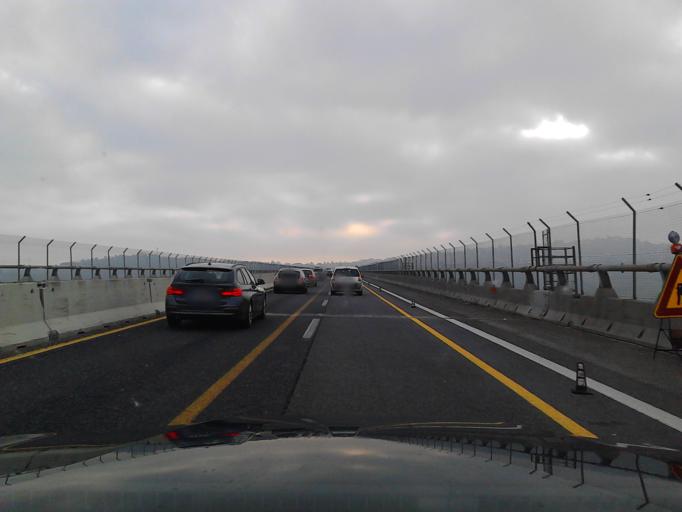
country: IT
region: Abruzzo
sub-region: Provincia di Teramo
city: Tortoreto Lido
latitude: 42.7834
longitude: 13.9348
